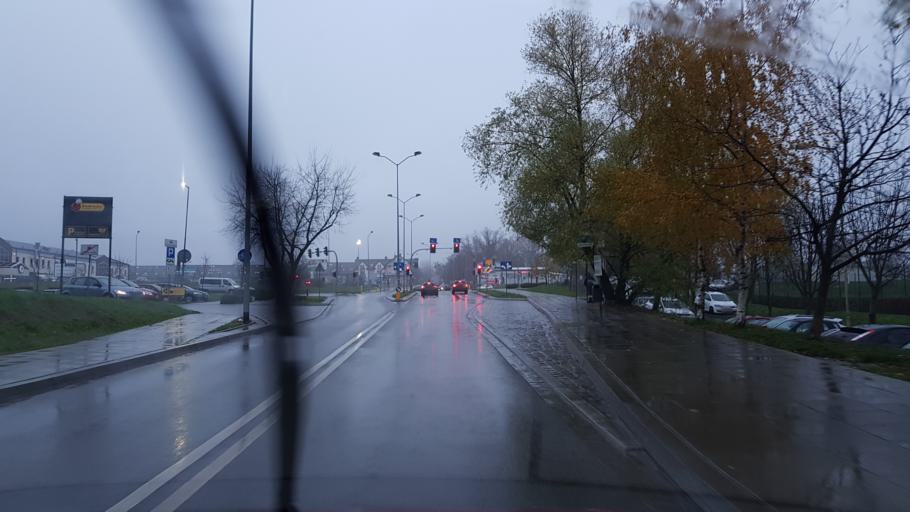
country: PL
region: West Pomeranian Voivodeship
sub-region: Szczecin
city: Szczecin
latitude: 53.4609
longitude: 14.5558
